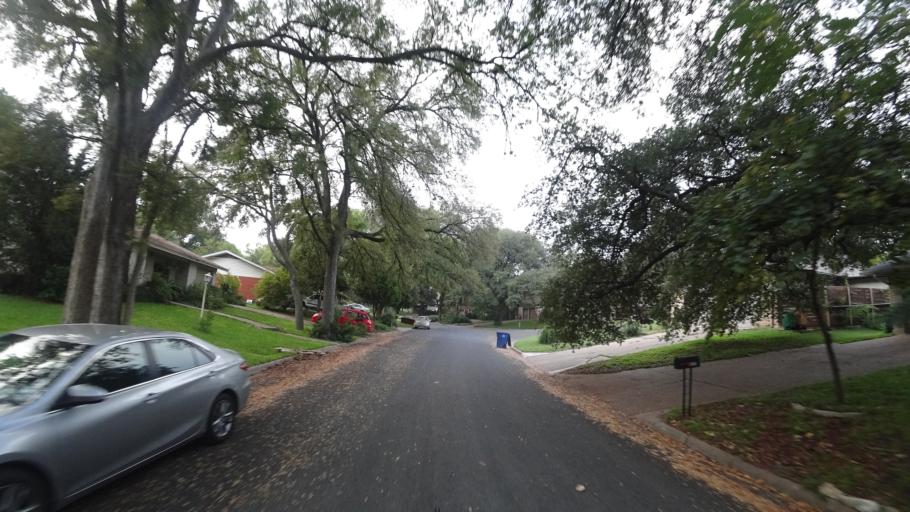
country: US
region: Texas
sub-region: Travis County
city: Austin
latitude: 30.3472
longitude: -97.6910
